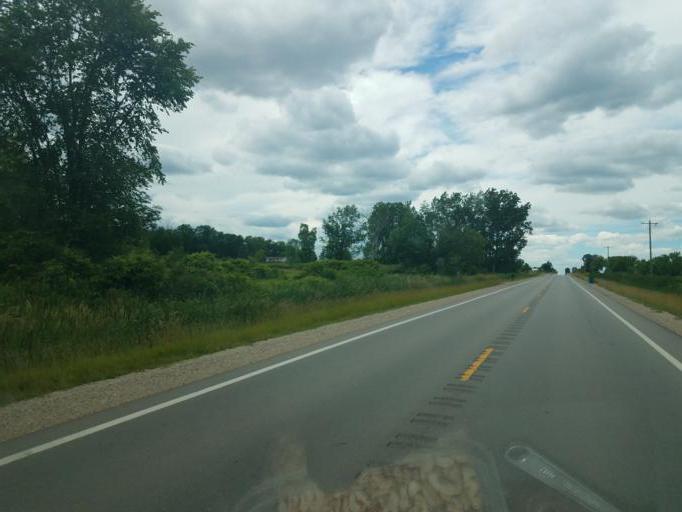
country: US
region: Michigan
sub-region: Eaton County
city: Charlotte
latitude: 42.6724
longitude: -84.9300
